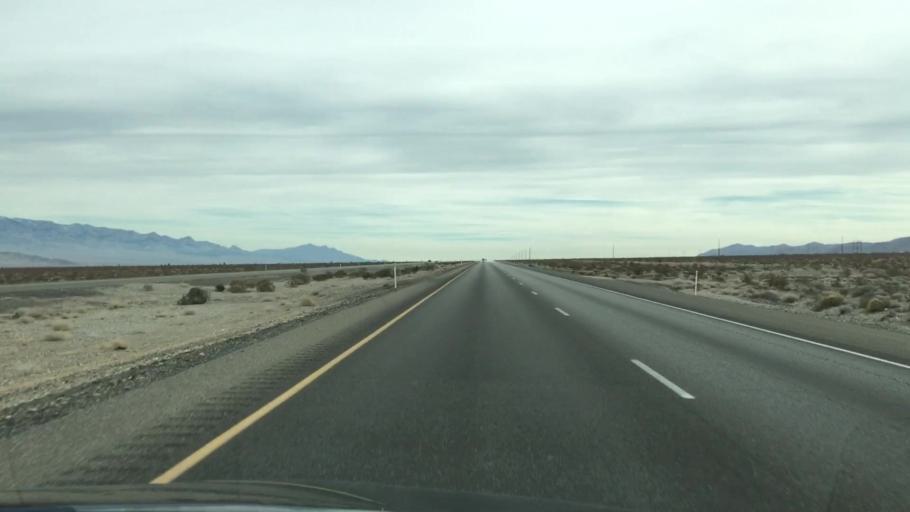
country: US
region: Nevada
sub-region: Nye County
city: Pahrump
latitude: 36.5688
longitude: -115.6261
